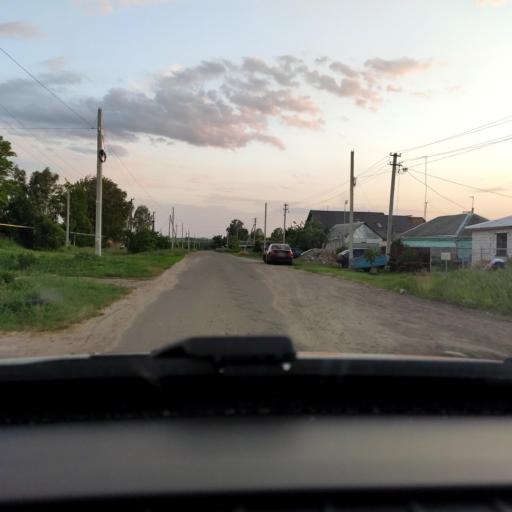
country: RU
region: Voronezj
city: Semiluki
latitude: 51.7485
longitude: 39.0243
